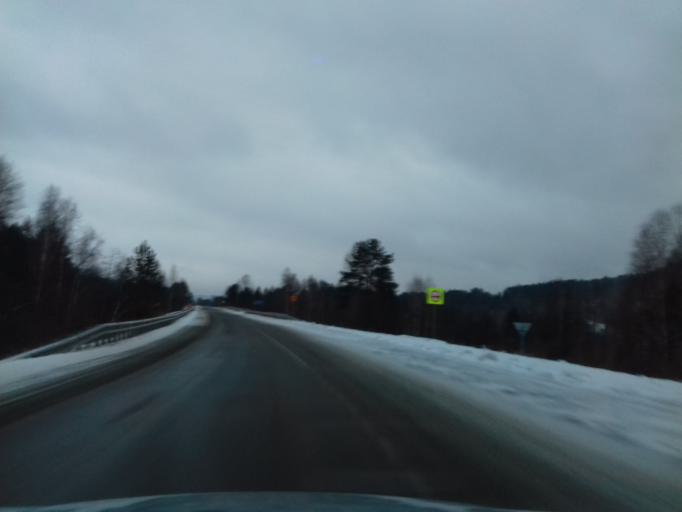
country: RU
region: Bashkortostan
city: Lomovka
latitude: 53.8042
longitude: 57.9510
